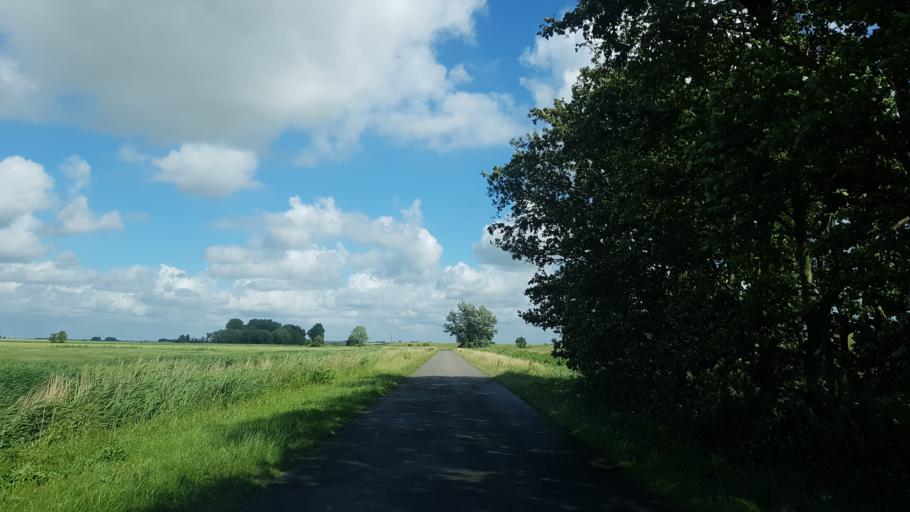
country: NL
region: Groningen
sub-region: Gemeente Winsum
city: Winsum
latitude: 53.4076
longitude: 6.5167
